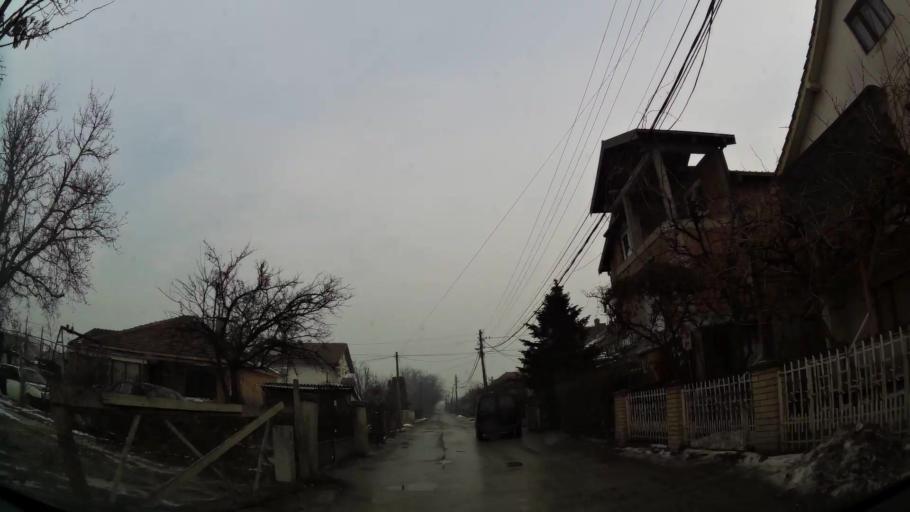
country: MK
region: Ilinden
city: Jurumleri
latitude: 41.9652
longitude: 21.5602
